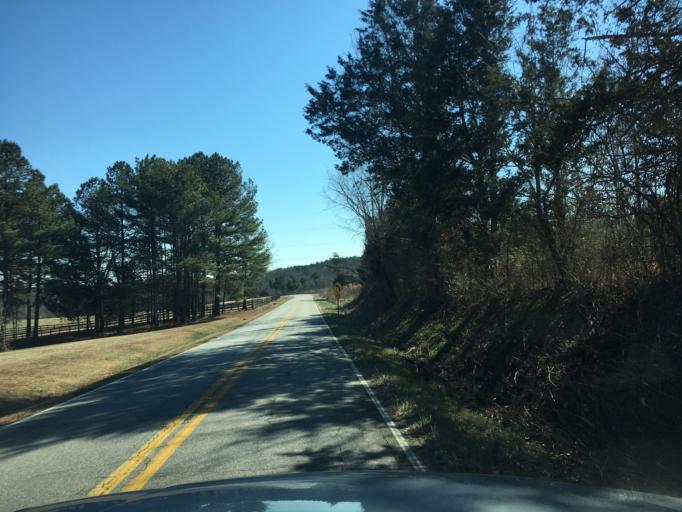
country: US
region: South Carolina
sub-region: Pickens County
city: Pickens
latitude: 34.8444
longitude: -82.8027
